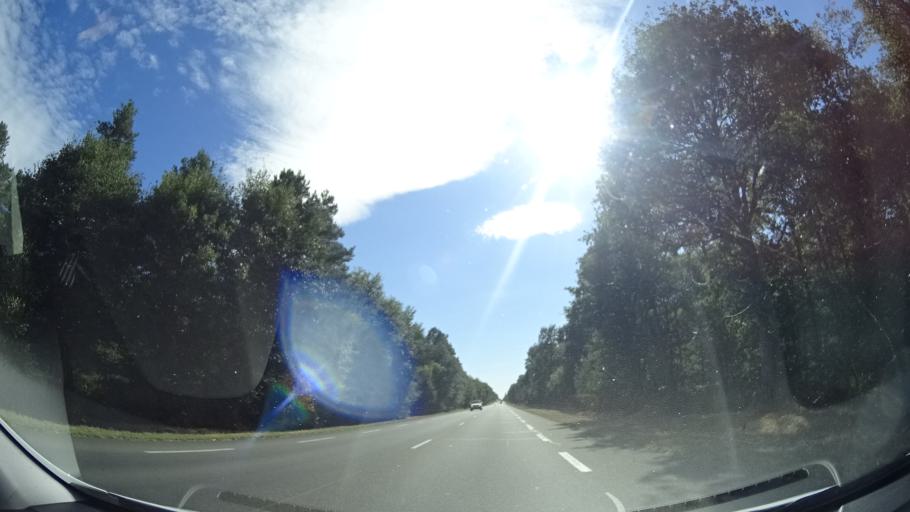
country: FR
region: Centre
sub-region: Departement du Loiret
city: Vitry-aux-Loges
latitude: 47.9232
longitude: 2.3255
